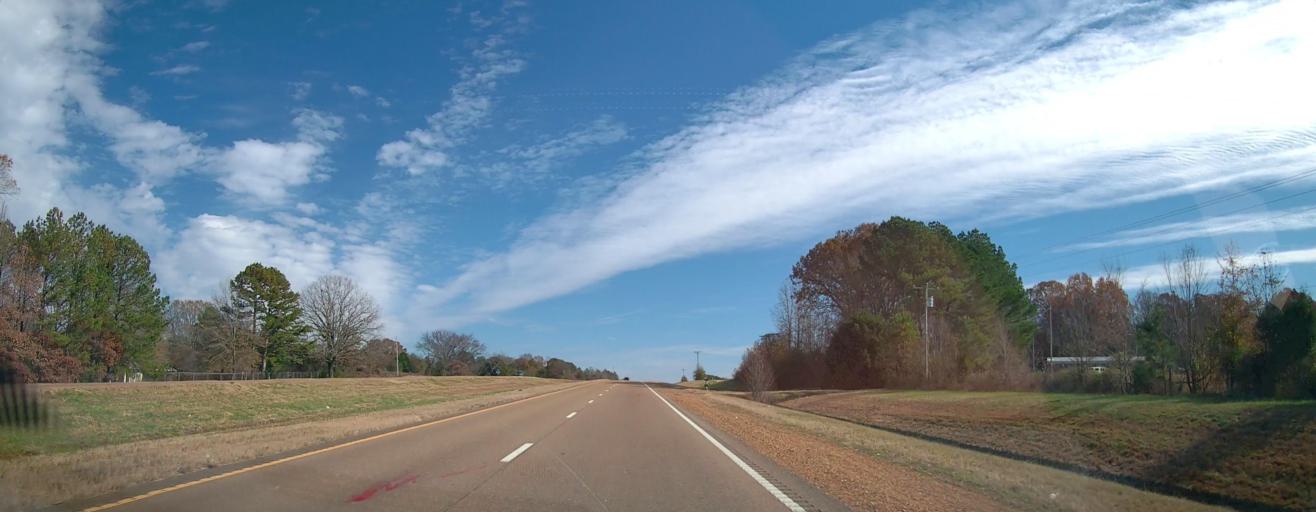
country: US
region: Mississippi
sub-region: Benton County
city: Ashland
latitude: 34.9459
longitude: -89.3278
